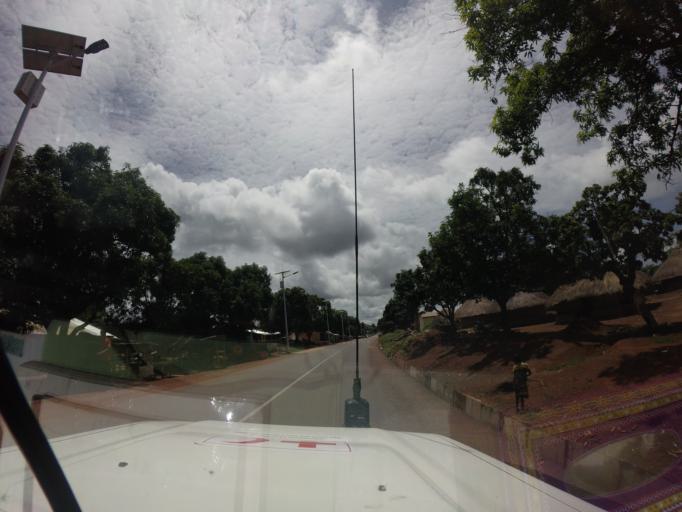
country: SL
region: Northern Province
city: Gberia Fotombu
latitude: 10.0662
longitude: -11.1208
